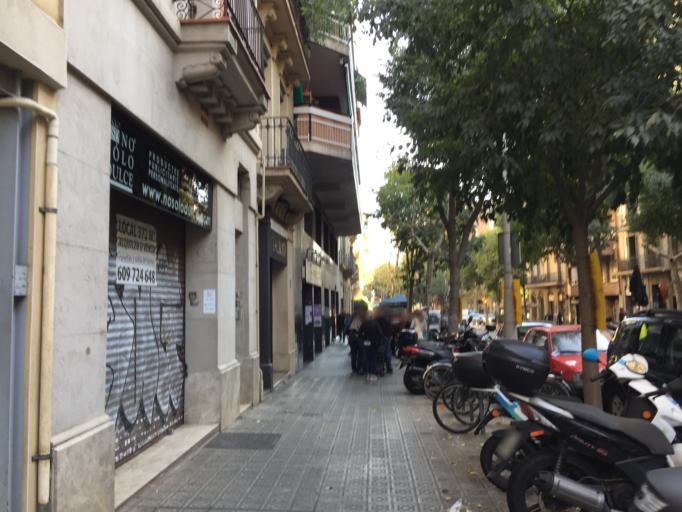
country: ES
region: Catalonia
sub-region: Provincia de Barcelona
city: Gracia
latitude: 41.4000
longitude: 2.1646
